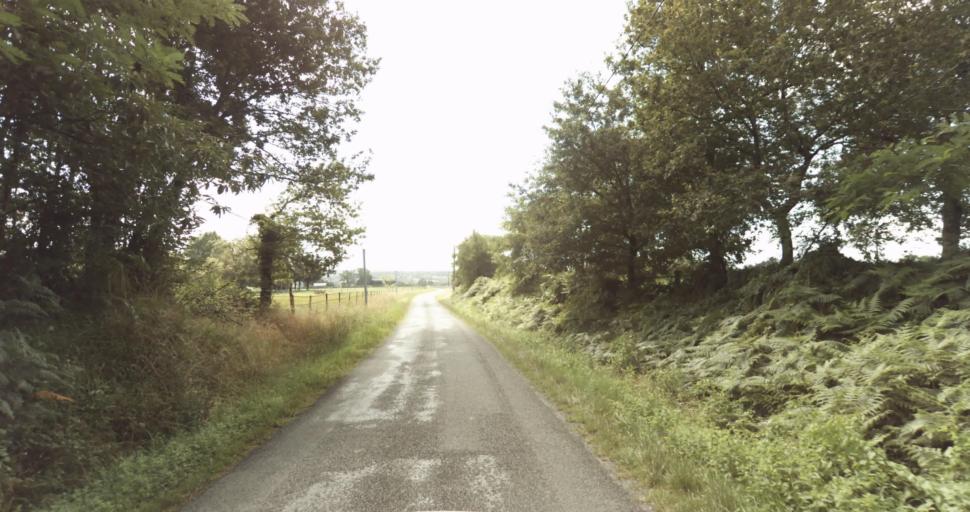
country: FR
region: Aquitaine
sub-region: Departement de la Gironde
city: Bazas
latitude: 44.4539
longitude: -0.1885
